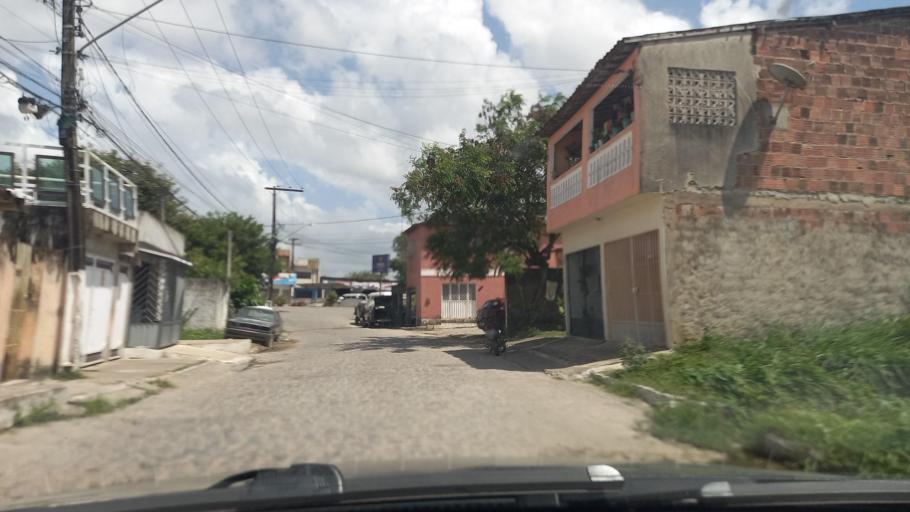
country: BR
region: Pernambuco
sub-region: Goiana
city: Goiana
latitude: -7.5662
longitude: -34.9977
